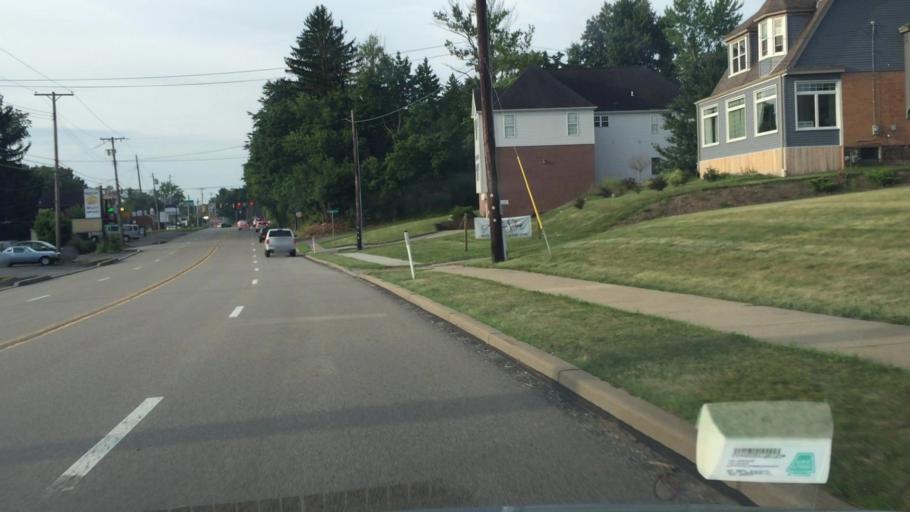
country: US
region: Pennsylvania
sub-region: Allegheny County
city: West View
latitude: 40.5585
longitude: -80.0397
